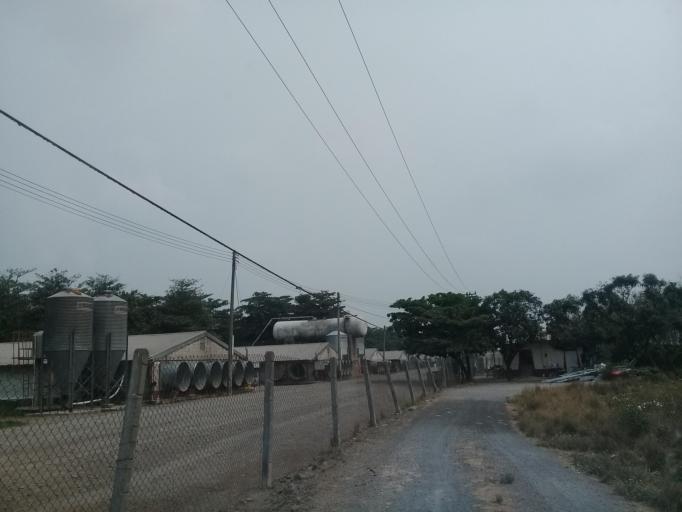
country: MX
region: Veracruz
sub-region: Medellin
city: La Laguna y Monte del Castillo
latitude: 18.9071
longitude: -96.1778
